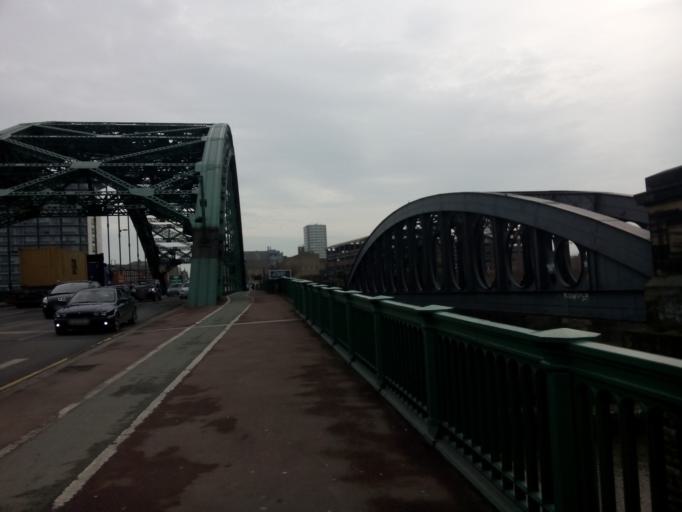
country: GB
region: England
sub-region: Sunderland
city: Sunderland
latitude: 54.9106
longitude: -1.3833
